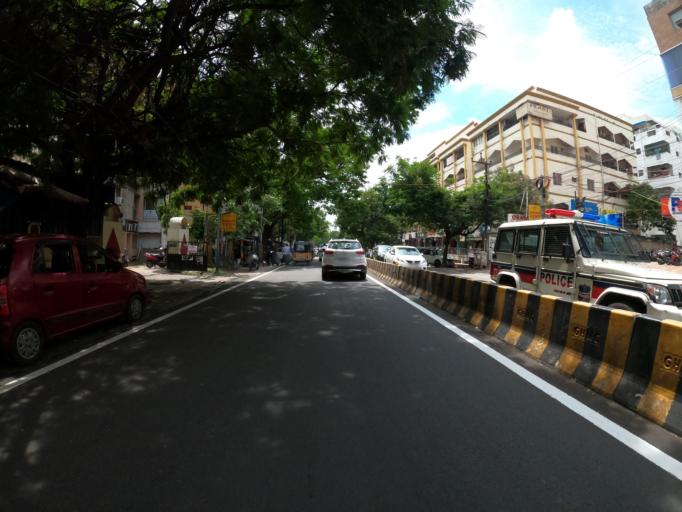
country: IN
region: Telangana
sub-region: Hyderabad
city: Hyderabad
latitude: 17.3987
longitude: 78.4814
